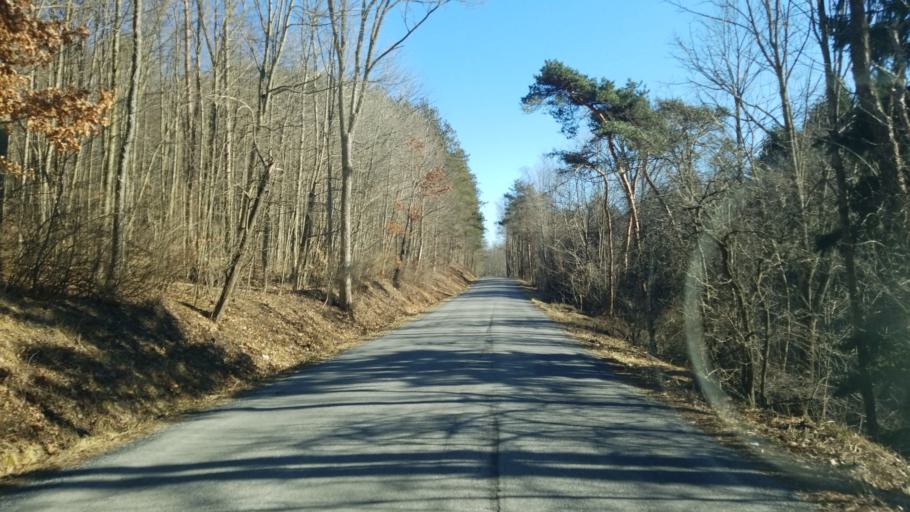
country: US
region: Pennsylvania
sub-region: Jefferson County
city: Sykesville
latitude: 41.0485
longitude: -78.7889
